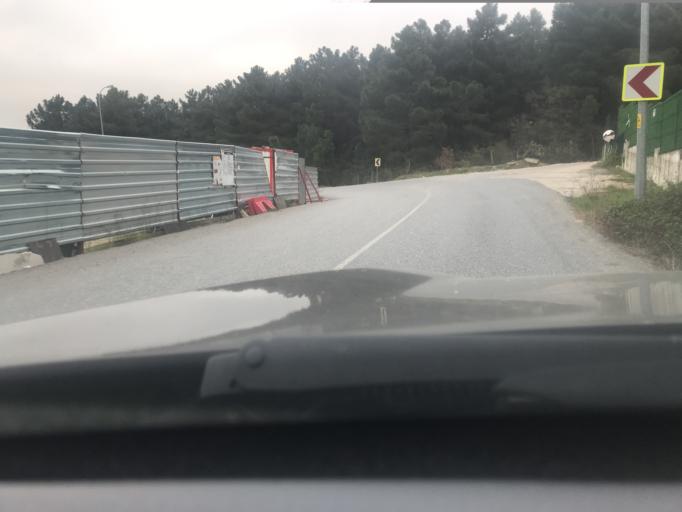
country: TR
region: Istanbul
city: Umraniye
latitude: 41.0427
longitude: 29.1603
